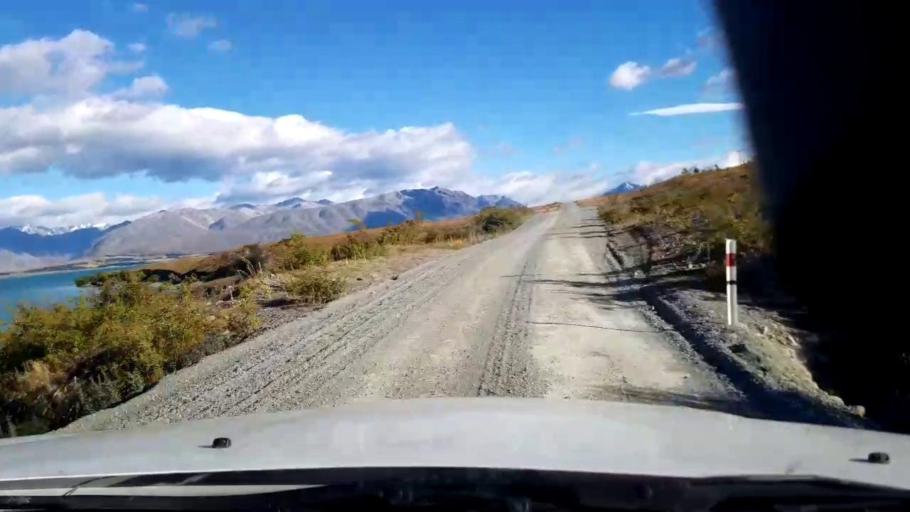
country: NZ
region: Canterbury
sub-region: Timaru District
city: Pleasant Point
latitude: -43.9254
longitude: 170.5602
